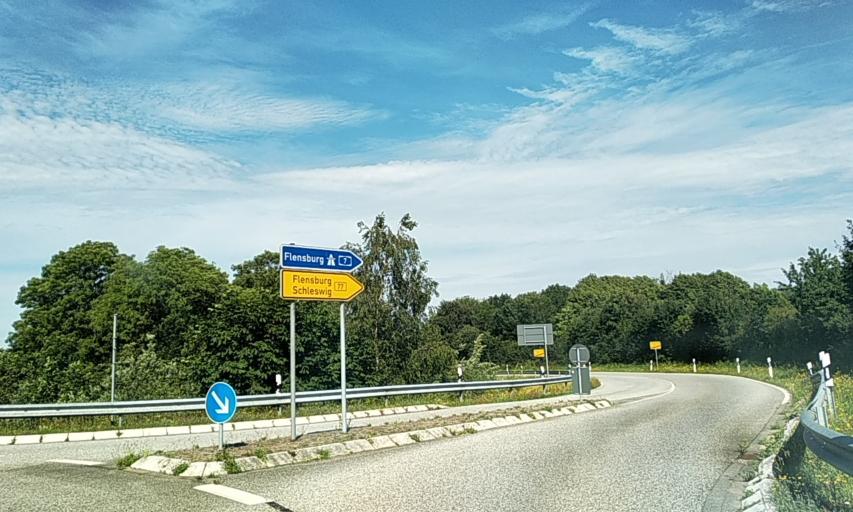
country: DE
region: Schleswig-Holstein
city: Fockbek
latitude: 54.3310
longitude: 9.6234
